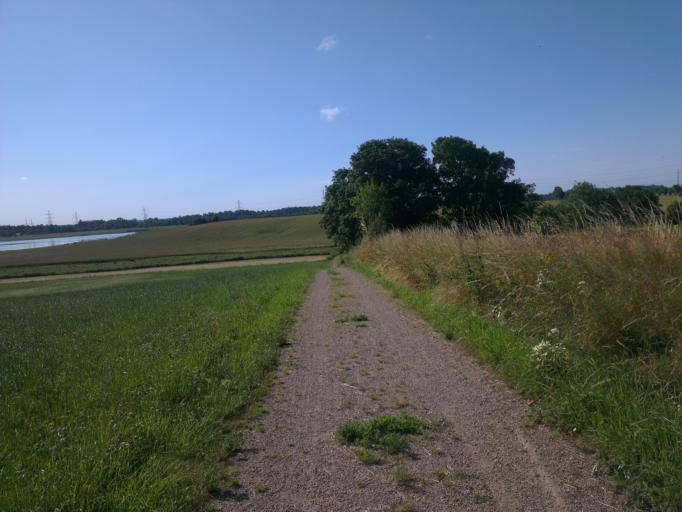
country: DK
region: Capital Region
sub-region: Frederikssund Kommune
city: Frederikssund
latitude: 55.8041
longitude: 12.0329
